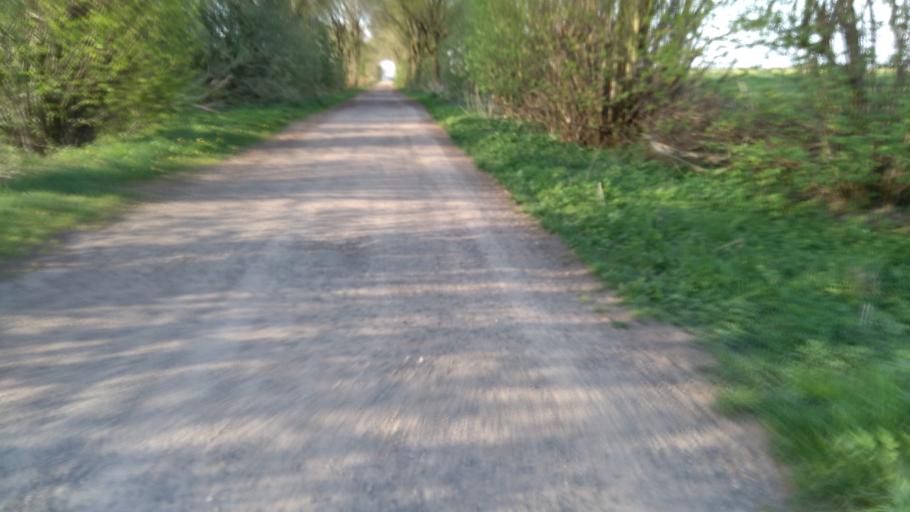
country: DE
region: Lower Saxony
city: Apensen
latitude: 53.4380
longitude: 9.6352
